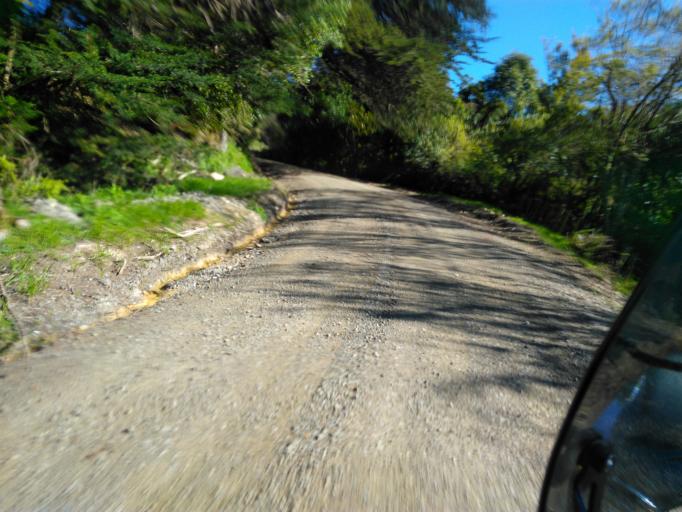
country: NZ
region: Bay of Plenty
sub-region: Opotiki District
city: Opotiki
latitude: -38.3680
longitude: 177.5979
